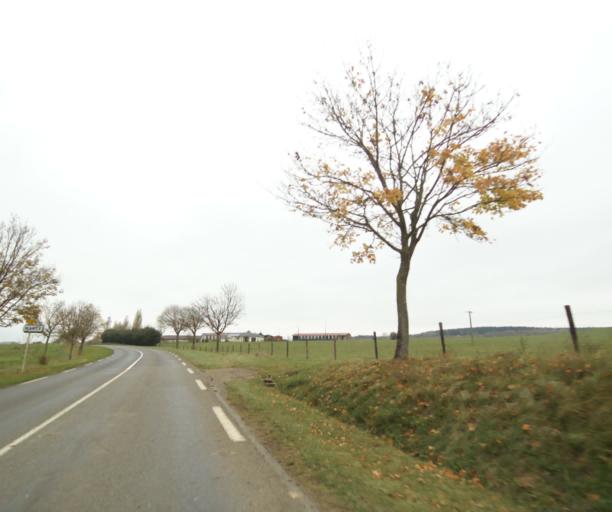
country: FR
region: Lorraine
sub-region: Departement de Meurthe-et-Moselle
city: Mancieulles
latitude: 49.2718
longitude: 5.9170
